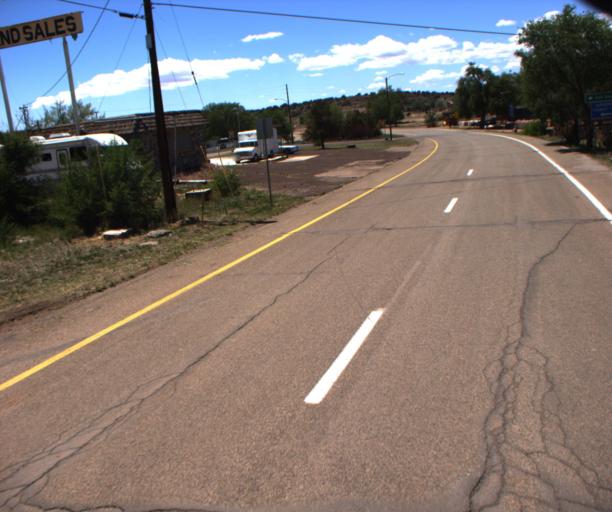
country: US
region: Arizona
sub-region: Coconino County
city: Williams
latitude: 35.2248
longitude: -112.4880
